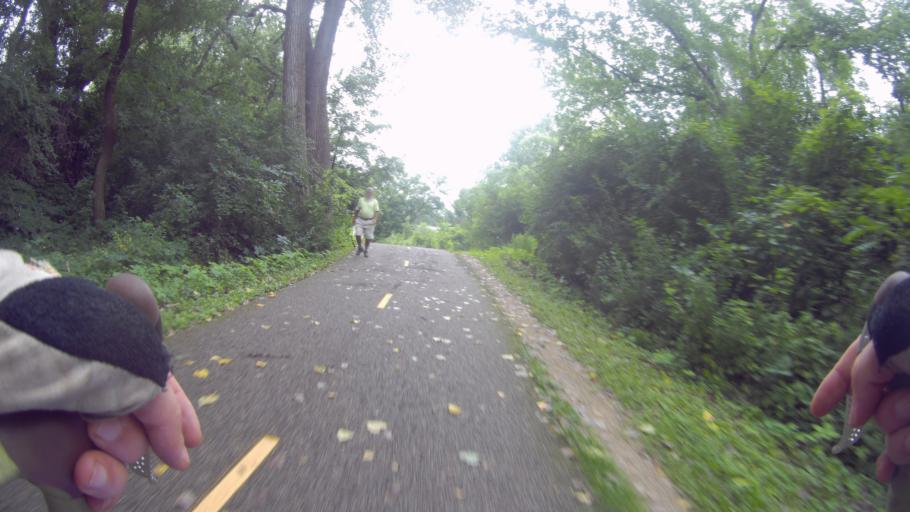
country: US
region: Wisconsin
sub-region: Dane County
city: Middleton
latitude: 43.1032
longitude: -89.5099
